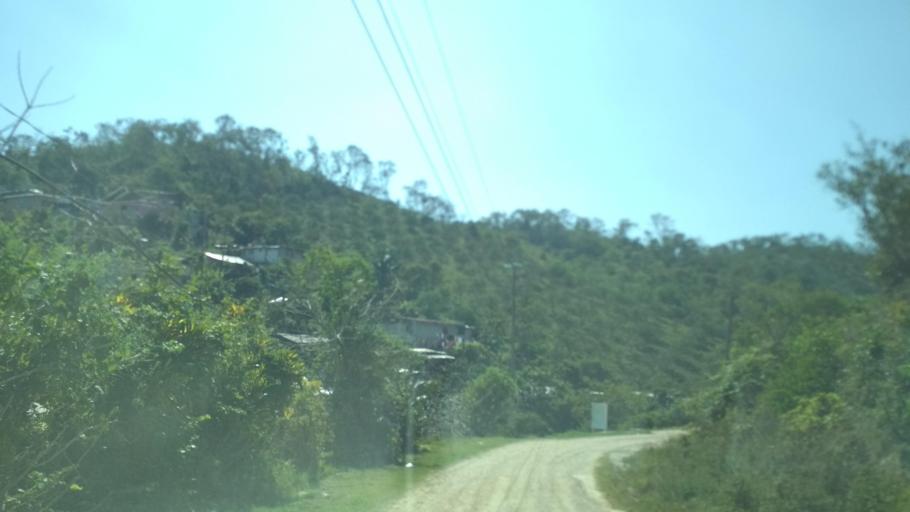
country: MX
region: Veracruz
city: Gutierrez Zamora
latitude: 20.4887
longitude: -97.1598
